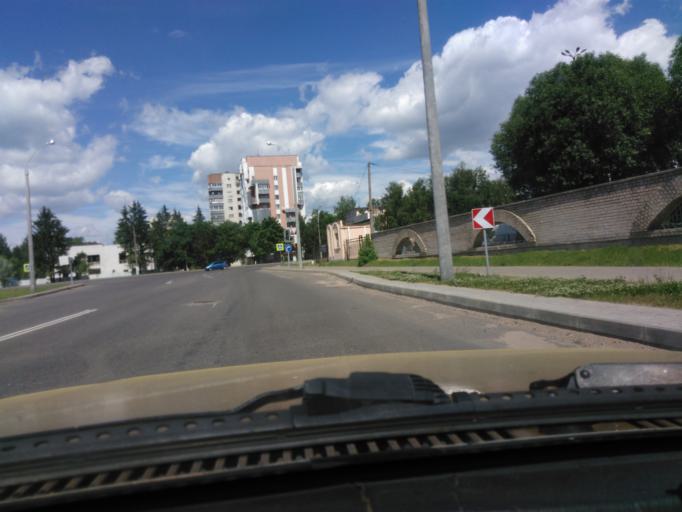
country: BY
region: Mogilev
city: Mahilyow
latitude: 53.9182
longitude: 30.3024
